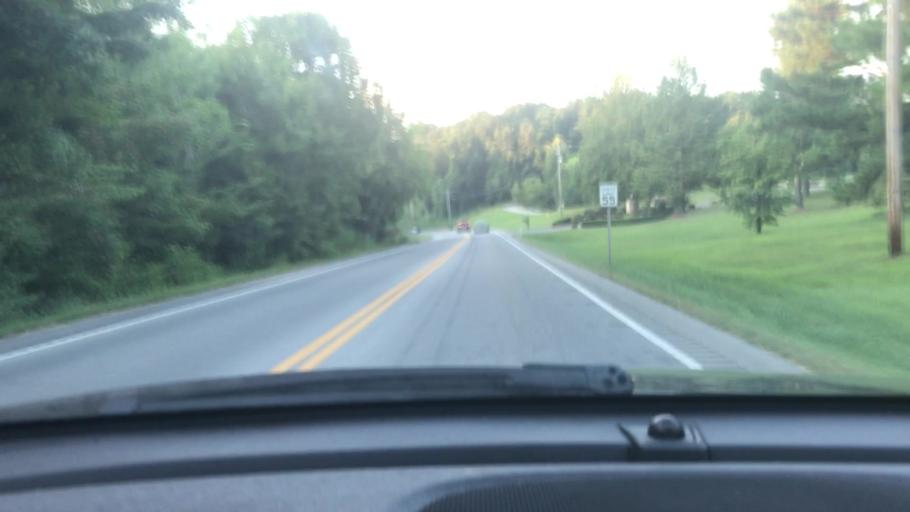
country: US
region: Tennessee
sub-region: Dickson County
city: Dickson
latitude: 36.1109
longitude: -87.3703
